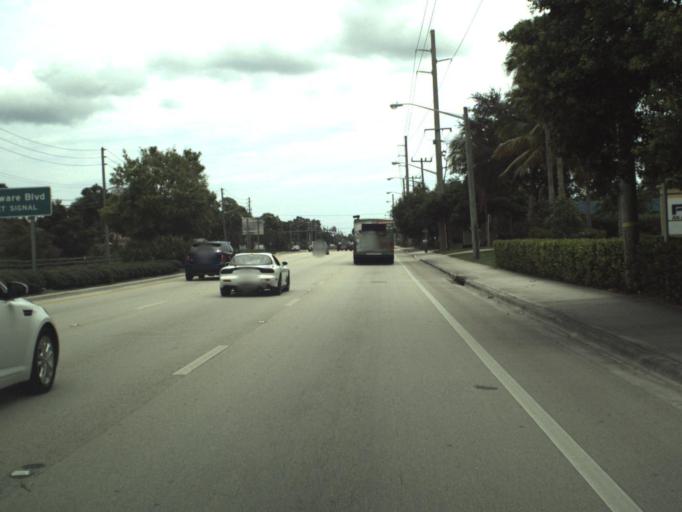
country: US
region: Florida
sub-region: Palm Beach County
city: Limestone Creek
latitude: 26.9341
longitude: -80.1216
